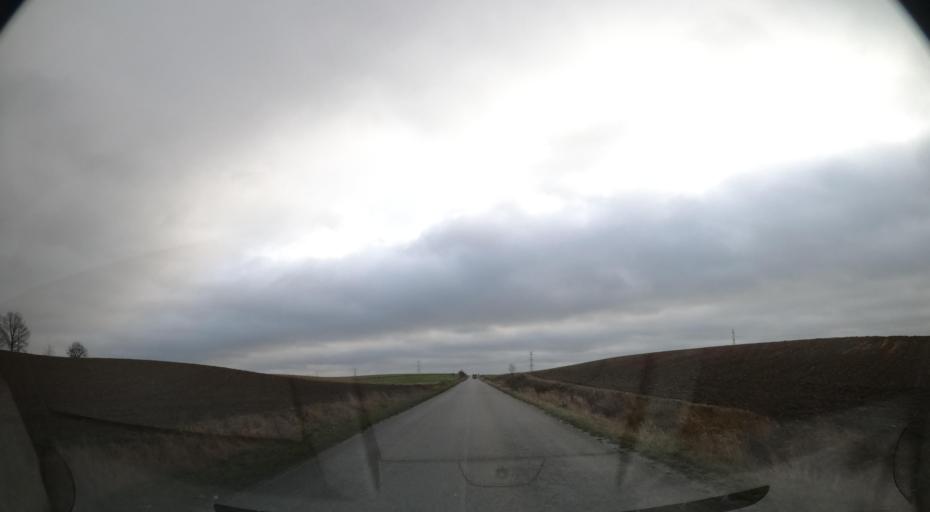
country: PL
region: Kujawsko-Pomorskie
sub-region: Powiat nakielski
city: Sadki
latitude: 53.1844
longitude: 17.4019
